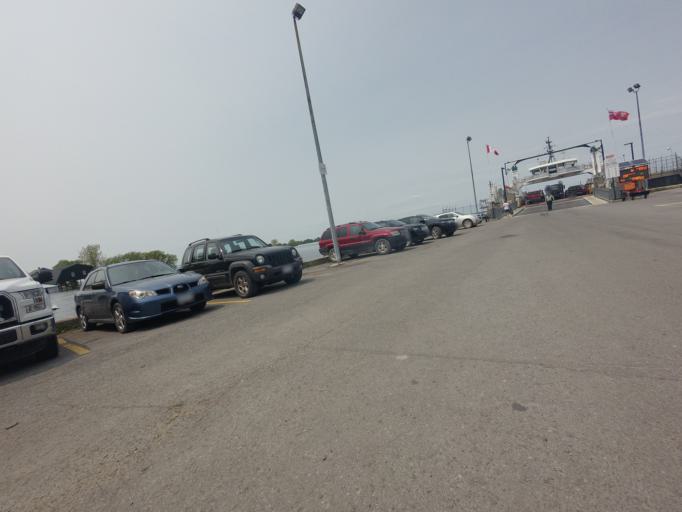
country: CA
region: Ontario
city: Kingston
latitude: 44.1943
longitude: -76.4408
